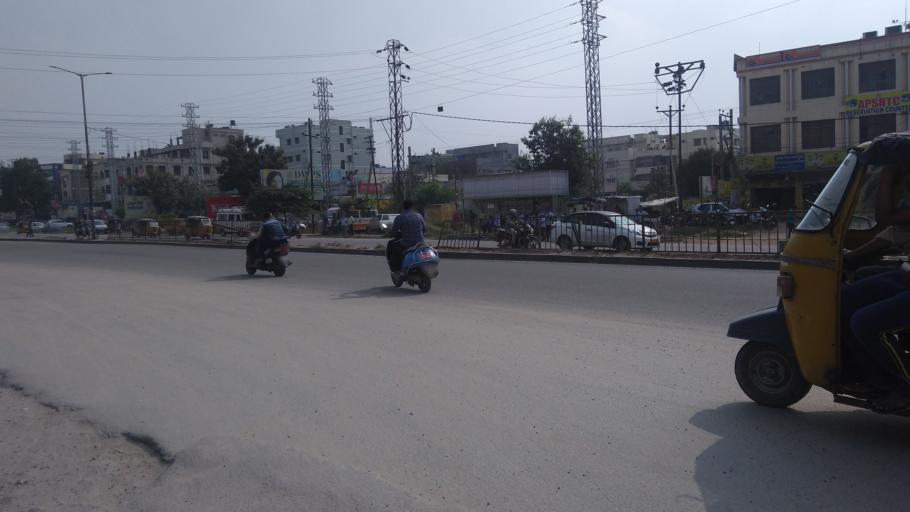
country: IN
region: Telangana
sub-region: Medak
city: Serilingampalle
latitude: 17.5097
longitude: 78.3006
